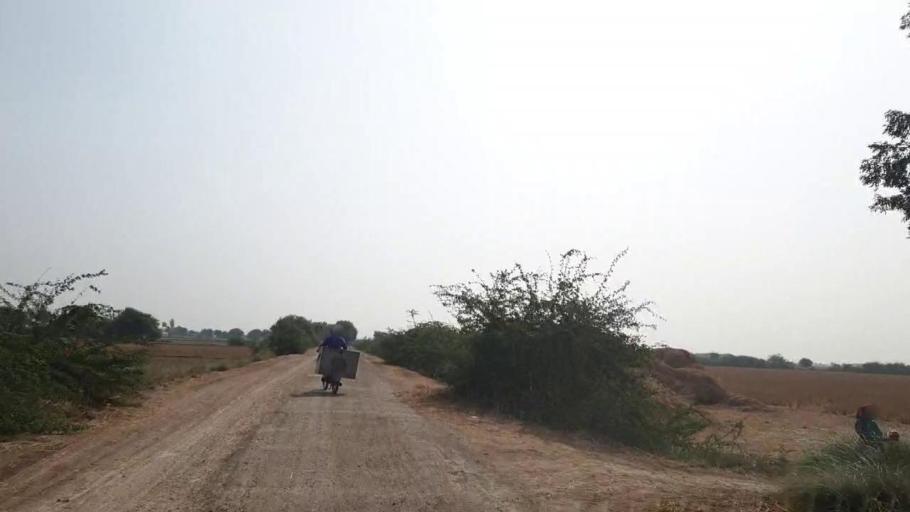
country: PK
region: Sindh
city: Matli
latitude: 24.9856
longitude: 68.5800
